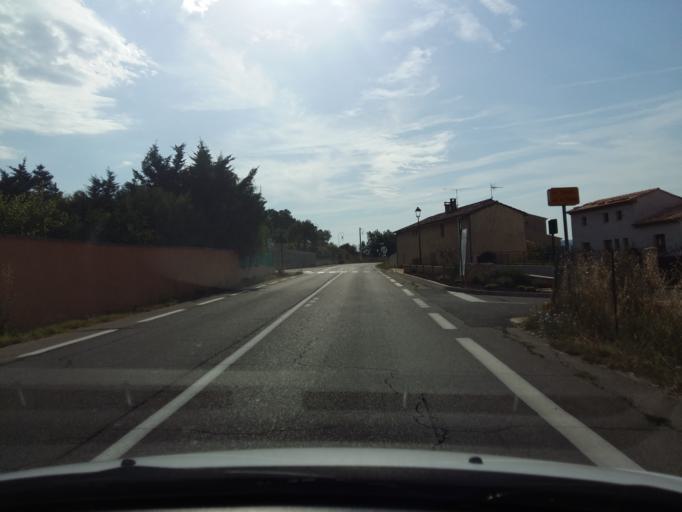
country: FR
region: Provence-Alpes-Cote d'Azur
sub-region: Departement du Vaucluse
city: Gargas
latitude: 43.8857
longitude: 5.3426
